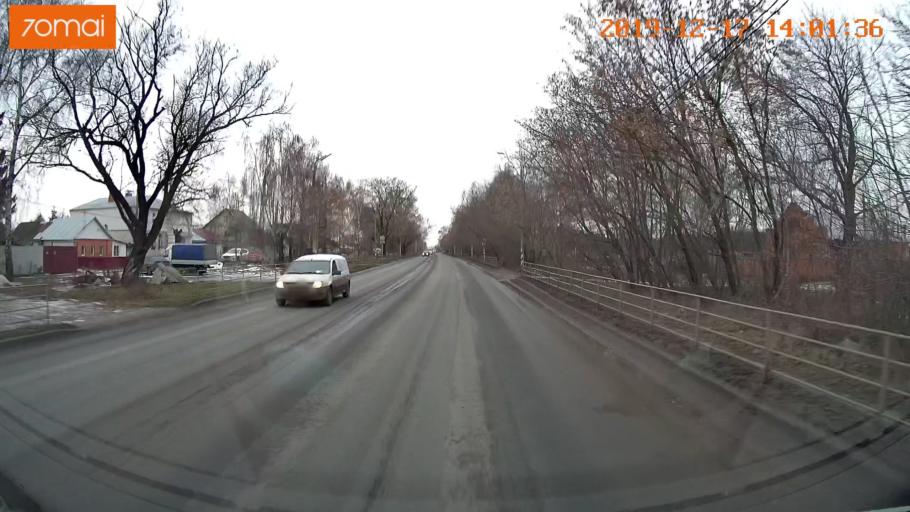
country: RU
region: Rjazan
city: Ryazan'
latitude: 54.6190
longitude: 39.6560
